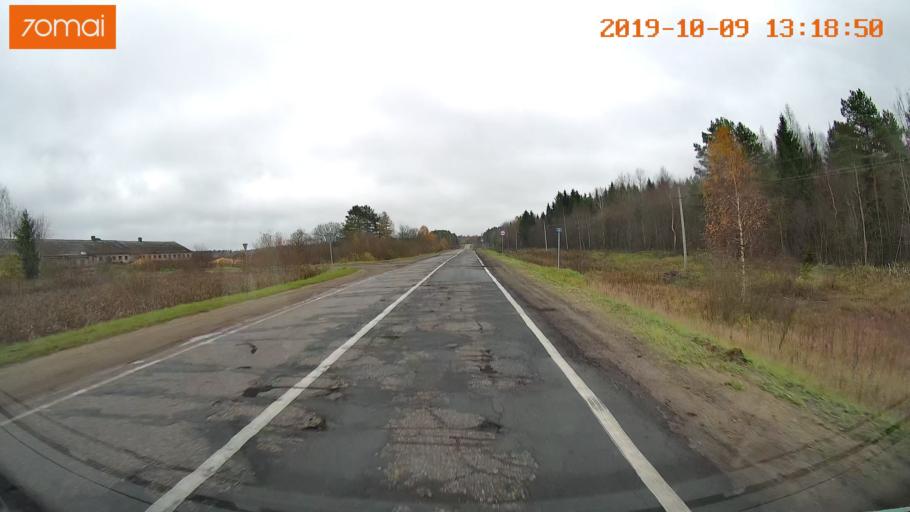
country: RU
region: Jaroslavl
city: Lyubim
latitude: 58.3502
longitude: 40.8020
